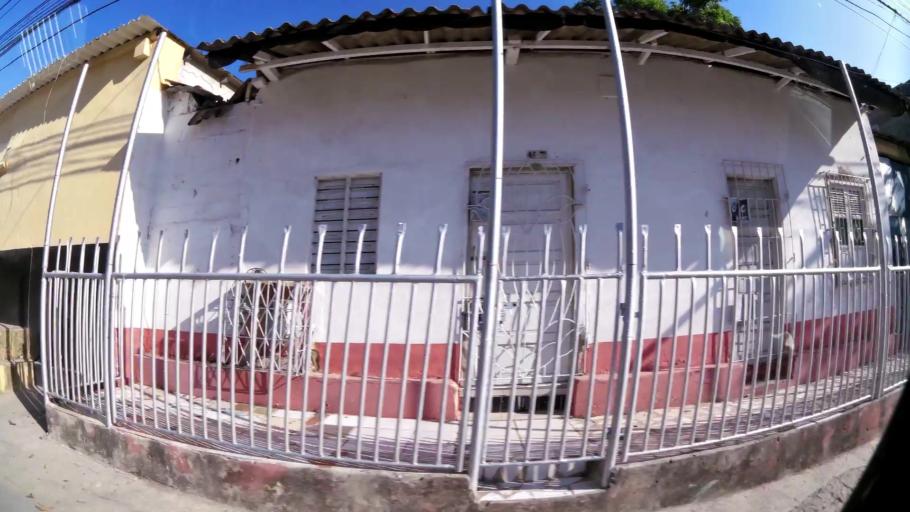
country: CO
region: Atlantico
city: Barranquilla
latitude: 10.9914
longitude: -74.7846
